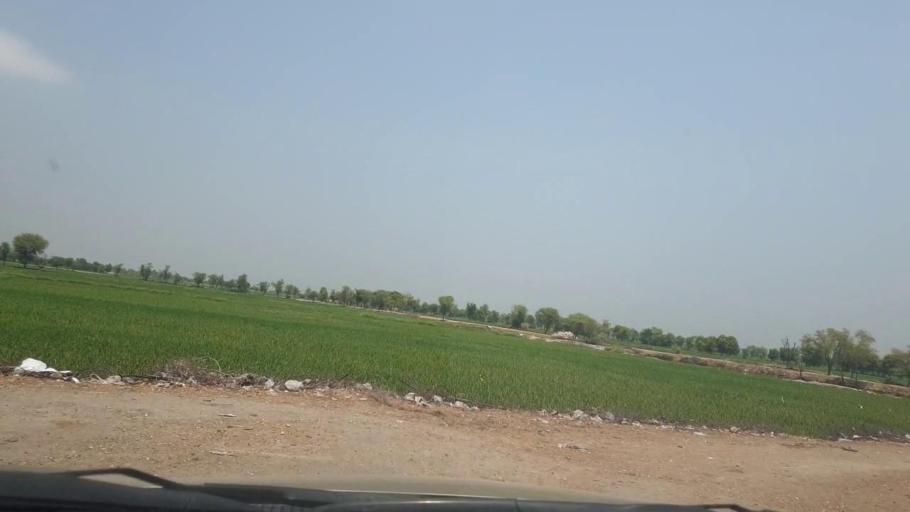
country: PK
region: Sindh
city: Ratodero
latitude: 27.7305
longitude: 68.2962
